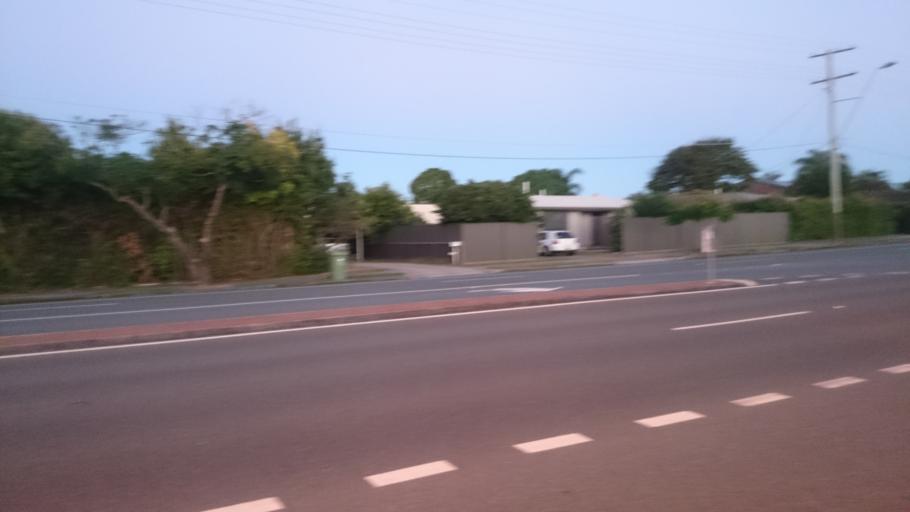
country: AU
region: Queensland
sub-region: Redland
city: Cleveland
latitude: -27.5319
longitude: 153.2666
